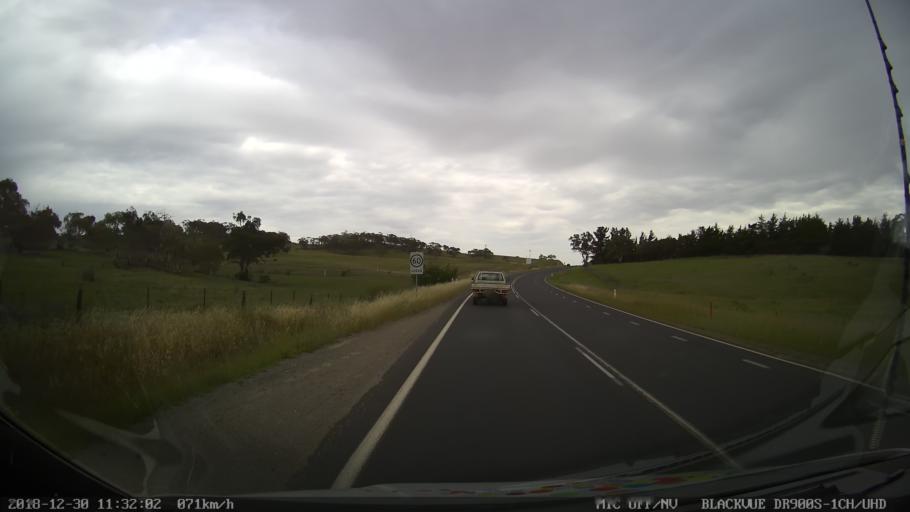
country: AU
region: New South Wales
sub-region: Snowy River
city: Jindabyne
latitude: -36.4254
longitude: 148.6090
